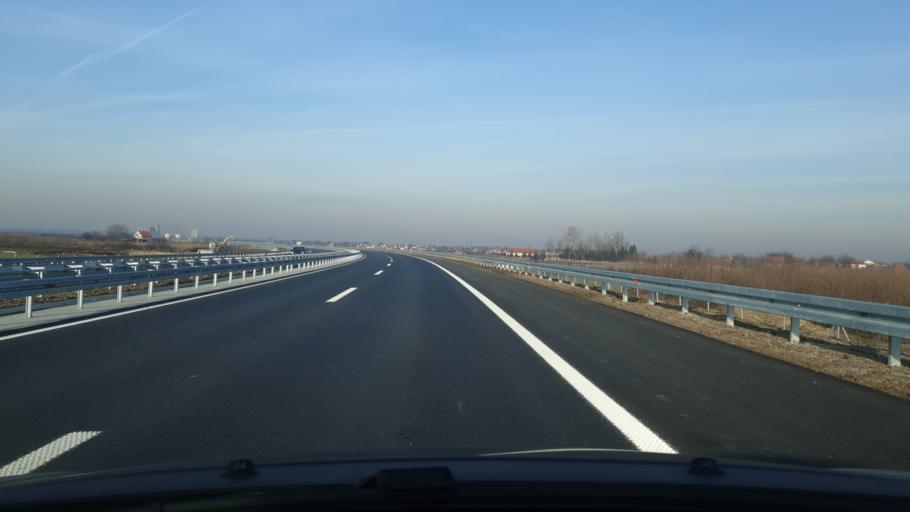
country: RS
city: Boljevci
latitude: 44.7484
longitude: 20.2503
